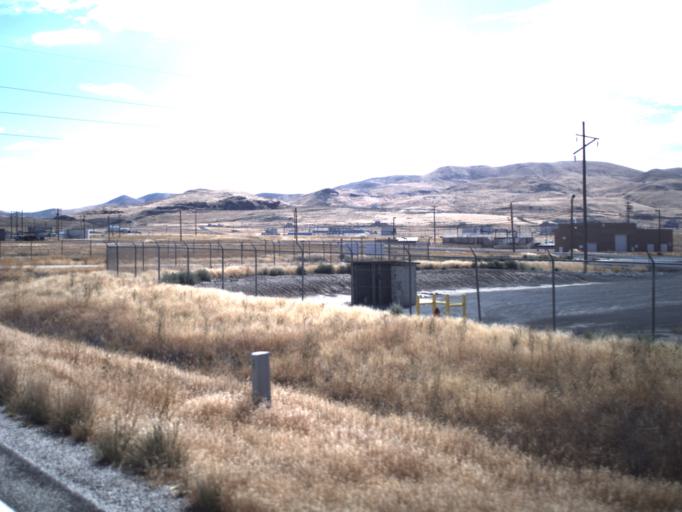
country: US
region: Utah
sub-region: Box Elder County
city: Tremonton
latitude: 41.7224
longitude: -112.4404
